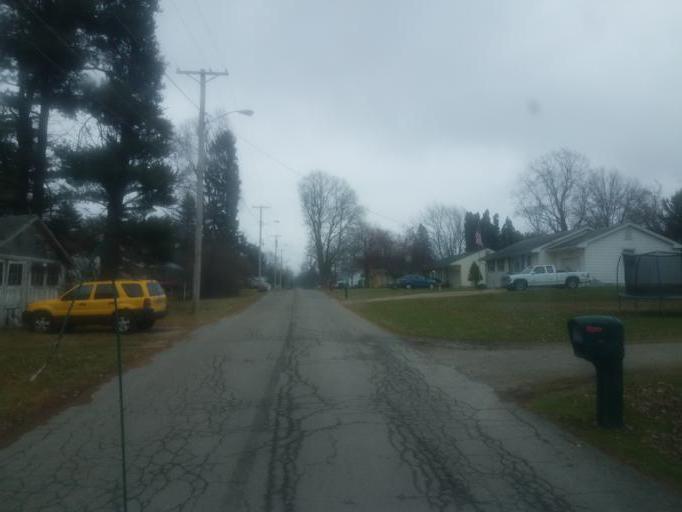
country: US
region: Ohio
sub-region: Crawford County
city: Galion
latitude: 40.7223
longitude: -82.7990
